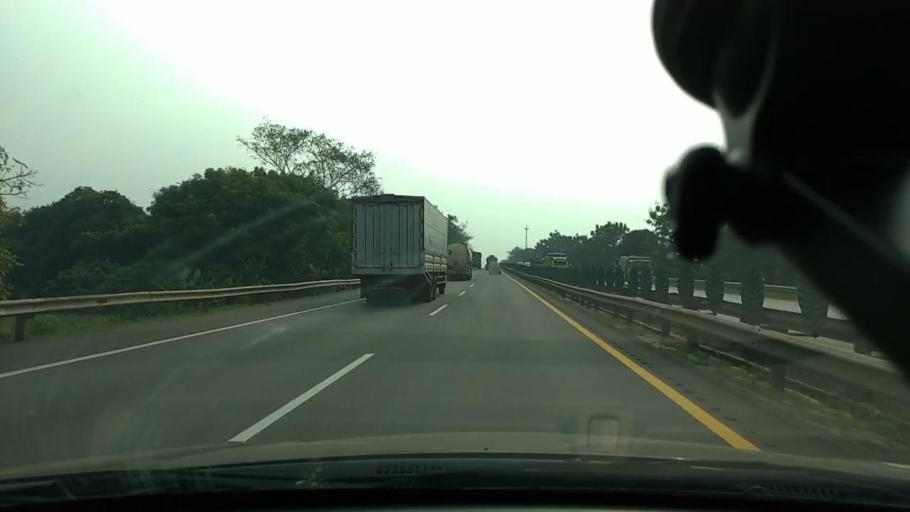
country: ID
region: Banten
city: Serang
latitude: -6.0939
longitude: 106.1611
